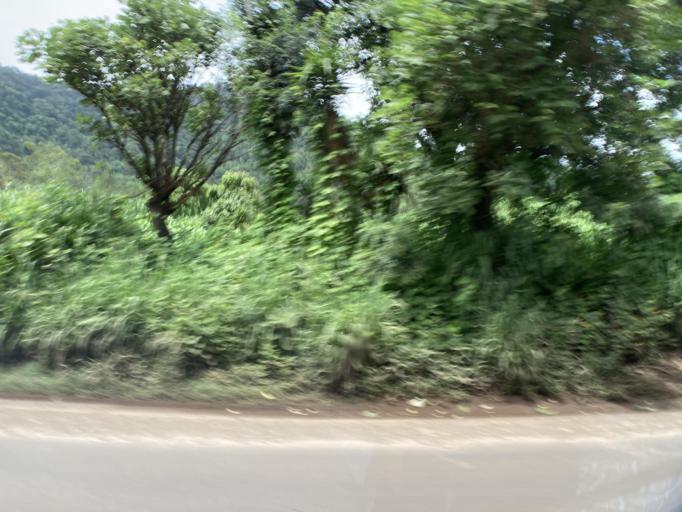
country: GT
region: Guatemala
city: Villa Canales
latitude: 14.4219
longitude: -90.5453
